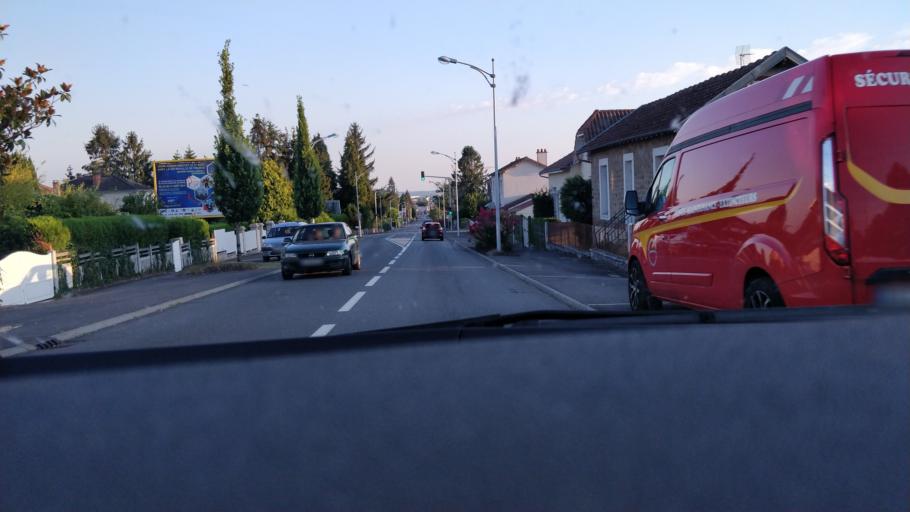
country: FR
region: Limousin
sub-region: Departement de la Haute-Vienne
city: Couzeix
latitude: 45.8685
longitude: 1.2383
